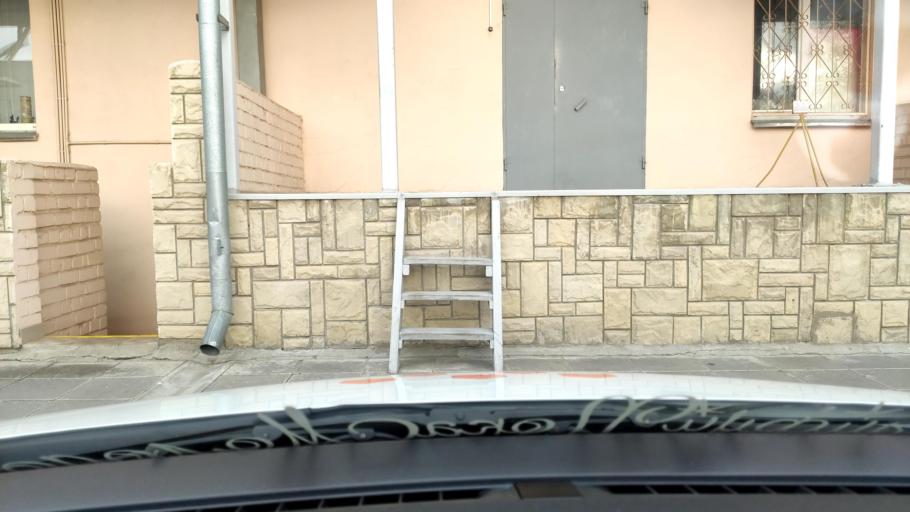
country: RU
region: Voronezj
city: Voronezh
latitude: 51.6853
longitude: 39.1730
